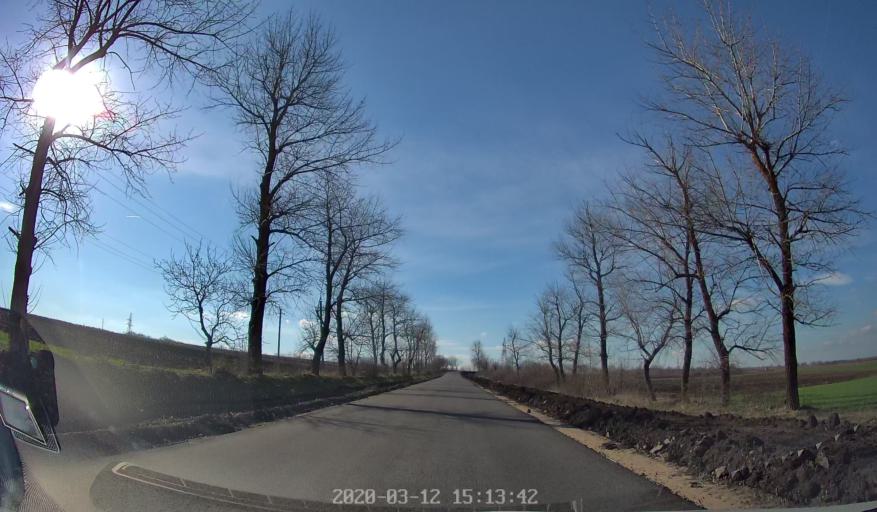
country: MD
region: Chisinau
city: Ciorescu
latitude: 47.2308
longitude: 28.9601
